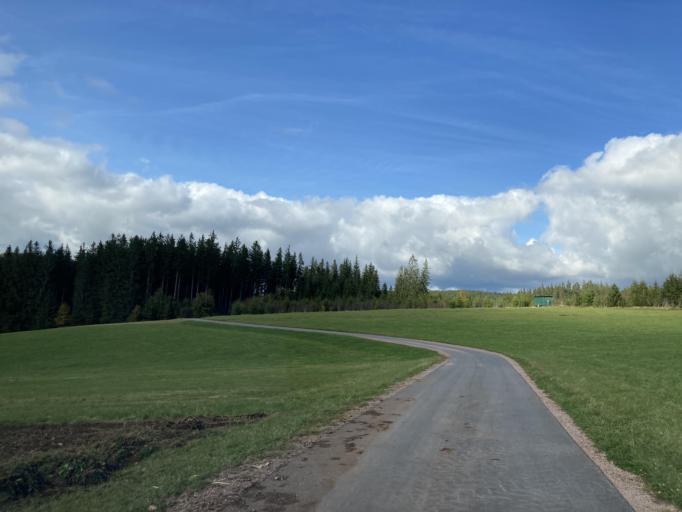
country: DE
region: Baden-Wuerttemberg
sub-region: Freiburg Region
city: Vohrenbach
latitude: 48.0812
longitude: 8.2796
